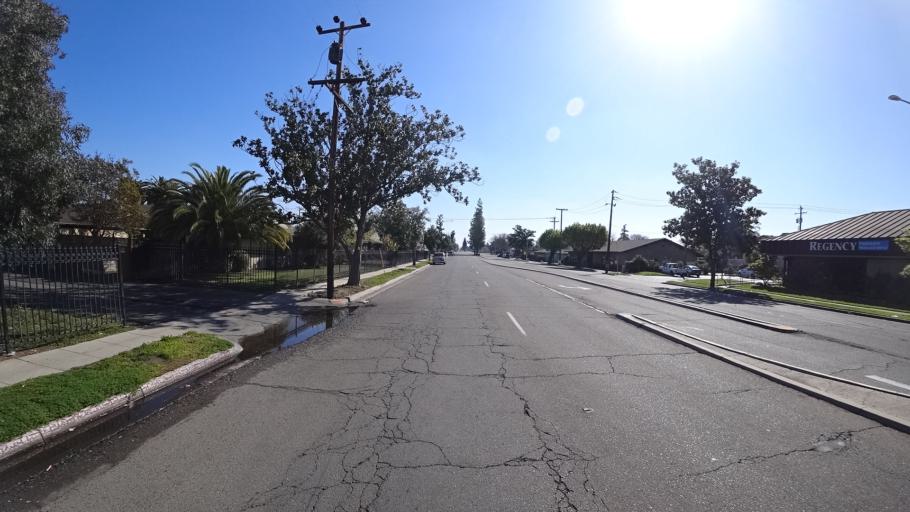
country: US
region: California
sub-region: Fresno County
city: Fresno
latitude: 36.7794
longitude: -119.8165
